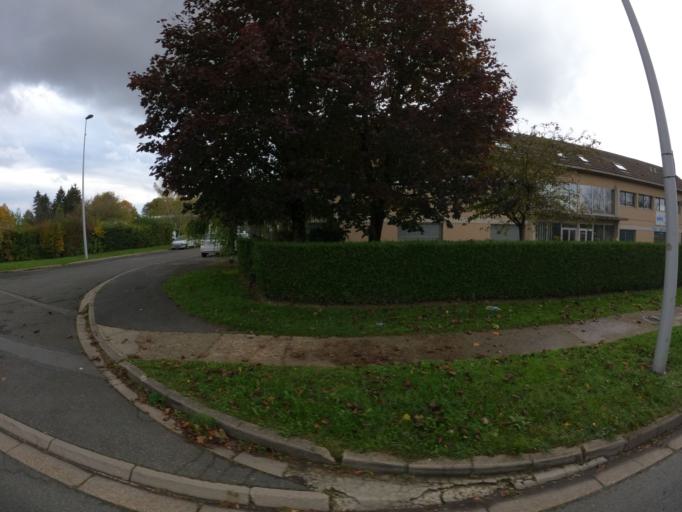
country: FR
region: Ile-de-France
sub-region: Departement de Seine-et-Marne
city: Emerainville
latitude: 48.8155
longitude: 2.6200
